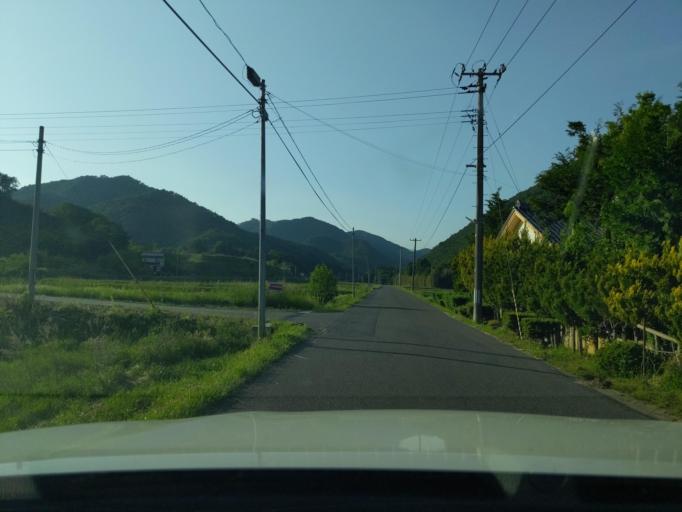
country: JP
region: Fukushima
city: Motomiya
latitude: 37.4925
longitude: 140.3285
